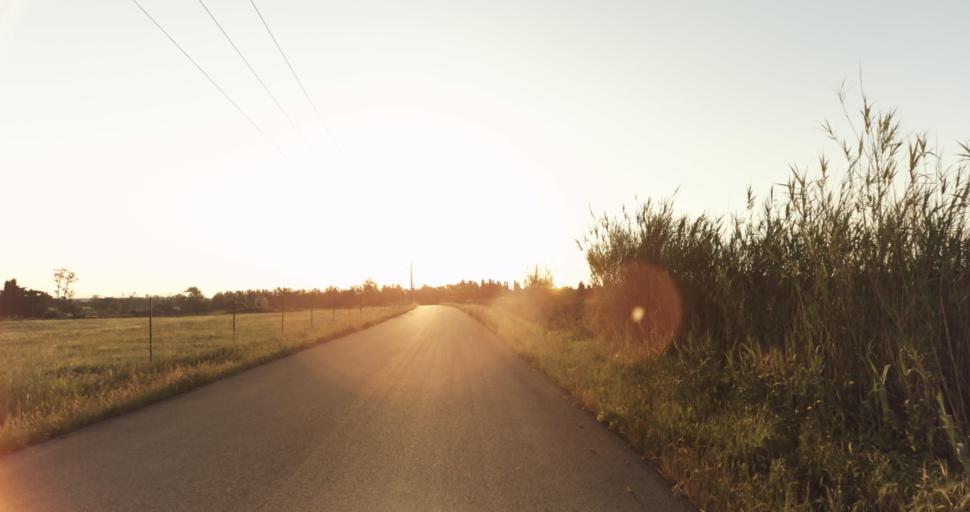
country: FR
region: Corsica
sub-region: Departement de la Haute-Corse
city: Biguglia
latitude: 42.5994
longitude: 9.4520
